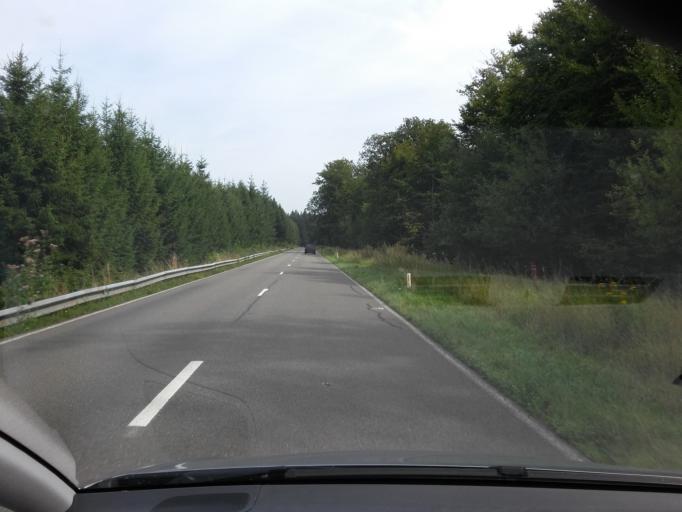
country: BE
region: Wallonia
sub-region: Province du Luxembourg
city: Chiny
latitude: 49.7698
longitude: 5.3237
